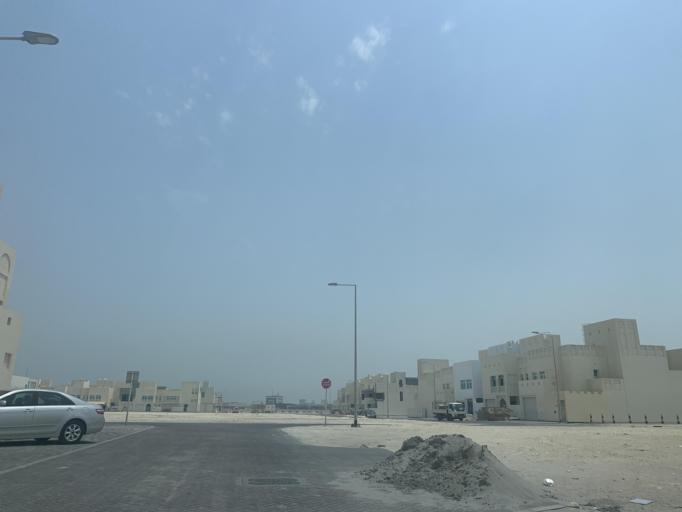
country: BH
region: Muharraq
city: Al Hadd
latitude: 26.2336
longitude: 50.6673
